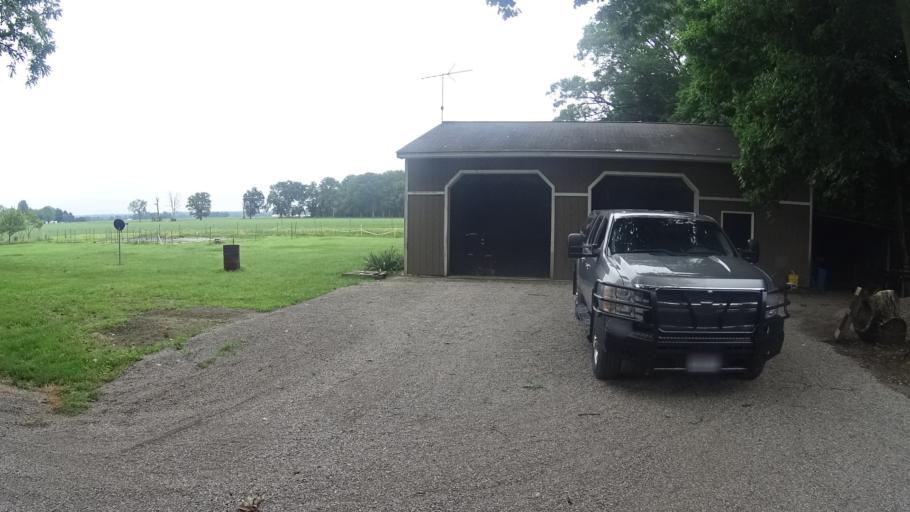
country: US
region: Ohio
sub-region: Erie County
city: Huron
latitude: 41.3471
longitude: -82.5524
